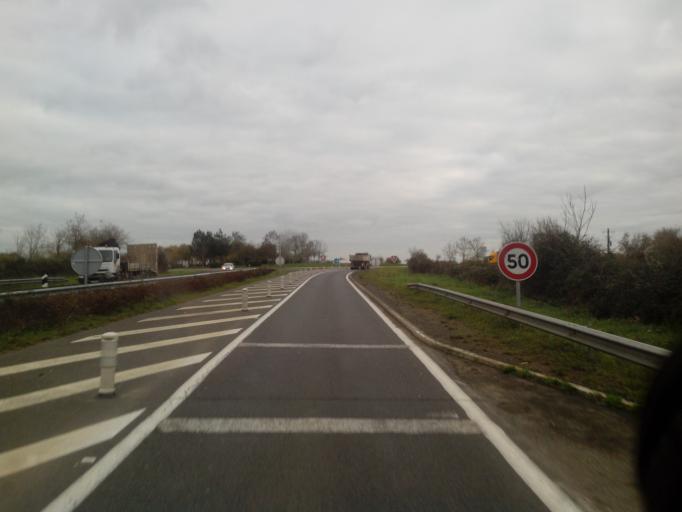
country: FR
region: Poitou-Charentes
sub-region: Departement des Deux-Sevres
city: Bressuire
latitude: 46.8342
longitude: -0.4383
